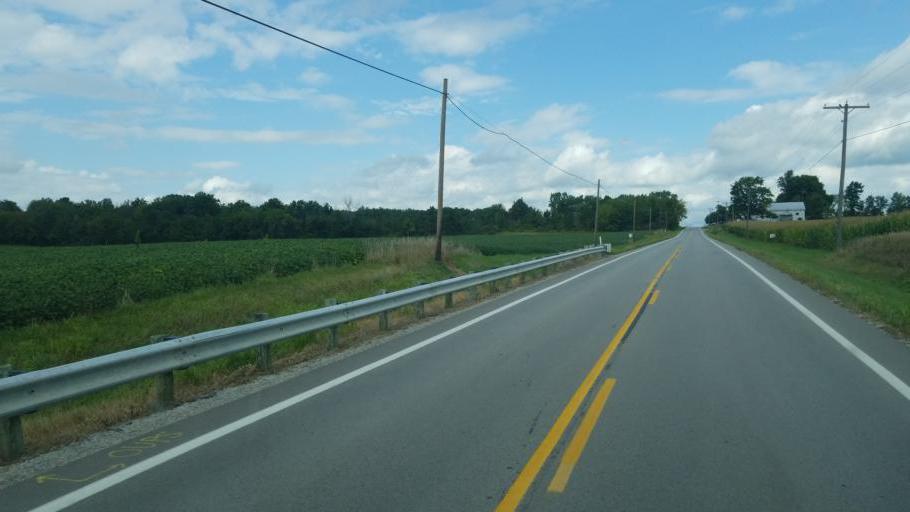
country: US
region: Ohio
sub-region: Seneca County
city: Tiffin
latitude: 41.0704
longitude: -83.0153
